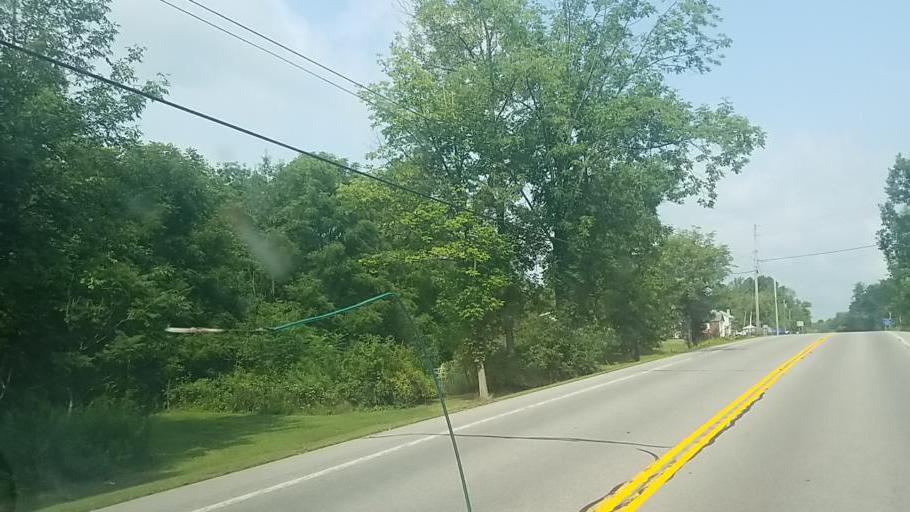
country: US
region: New York
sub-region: Montgomery County
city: Saint Johnsville
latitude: 42.9792
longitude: -74.6396
